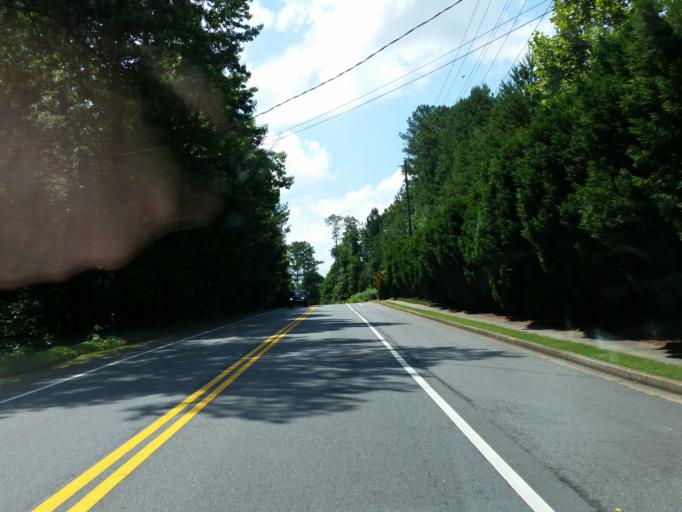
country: US
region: Georgia
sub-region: Fulton County
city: Roswell
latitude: 34.0285
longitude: -84.3912
